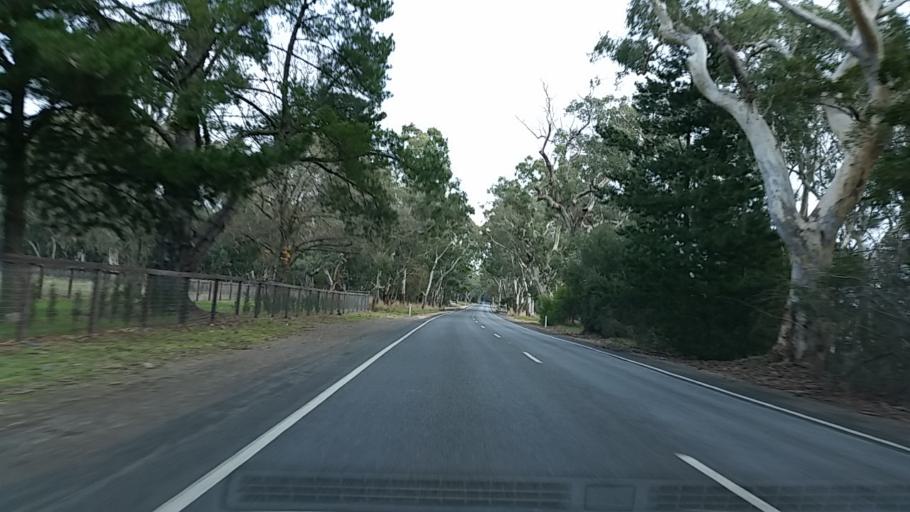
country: AU
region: South Australia
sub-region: Mount Barker
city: Meadows
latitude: -35.1998
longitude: 138.7192
